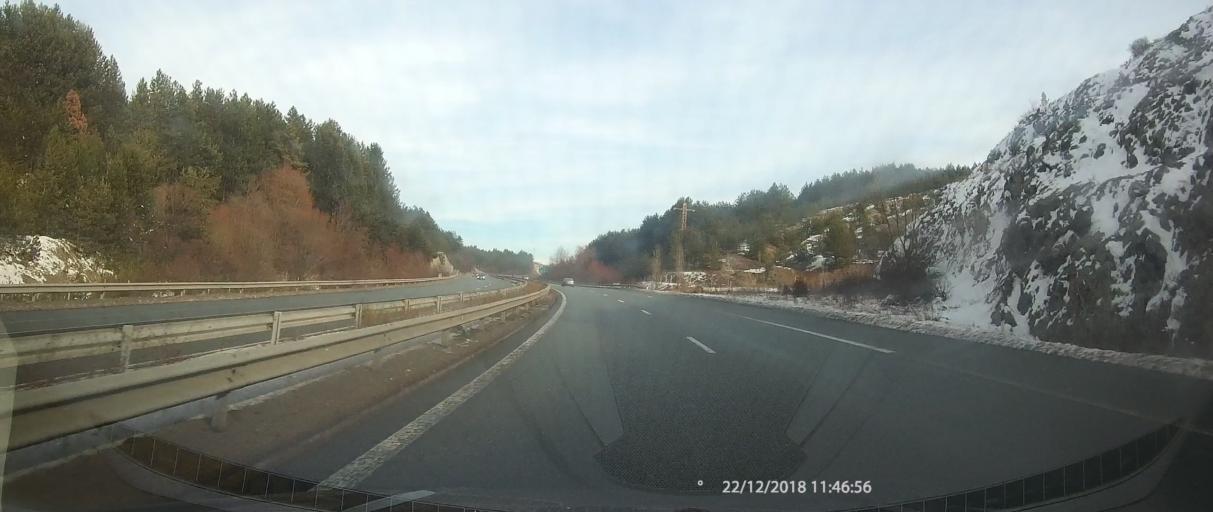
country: BG
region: Pernik
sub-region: Obshtina Pernik
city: Pernik
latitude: 42.4919
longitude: 23.1328
